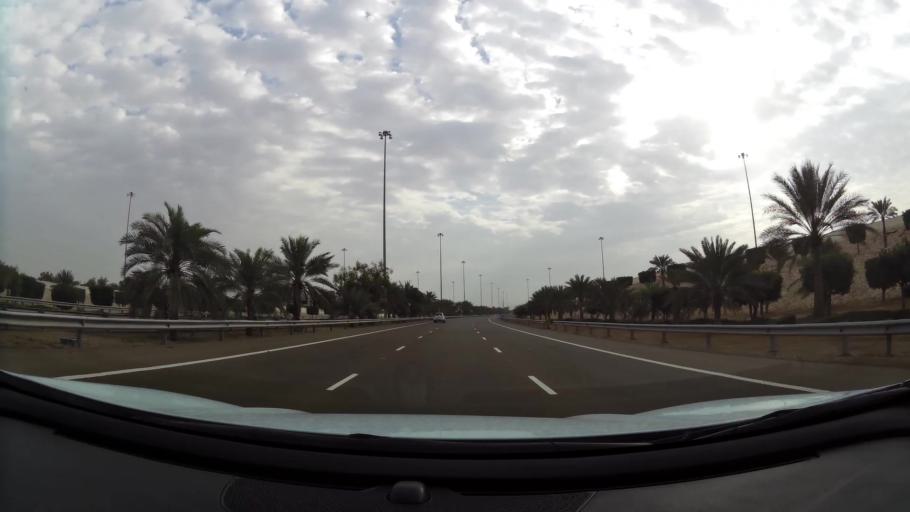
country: AE
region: Abu Dhabi
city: Al Ain
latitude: 24.2038
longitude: 55.3873
